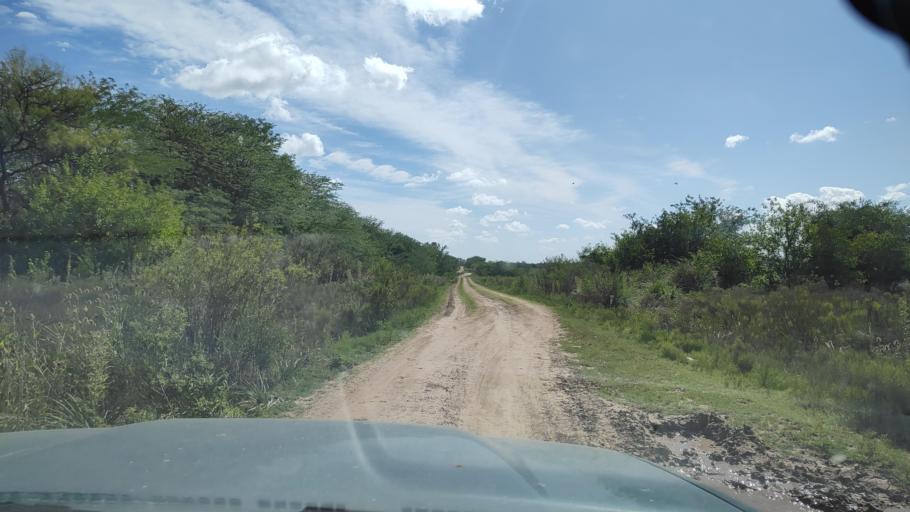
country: AR
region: Buenos Aires
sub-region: Partido de Lujan
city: Lujan
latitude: -34.5227
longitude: -59.1716
